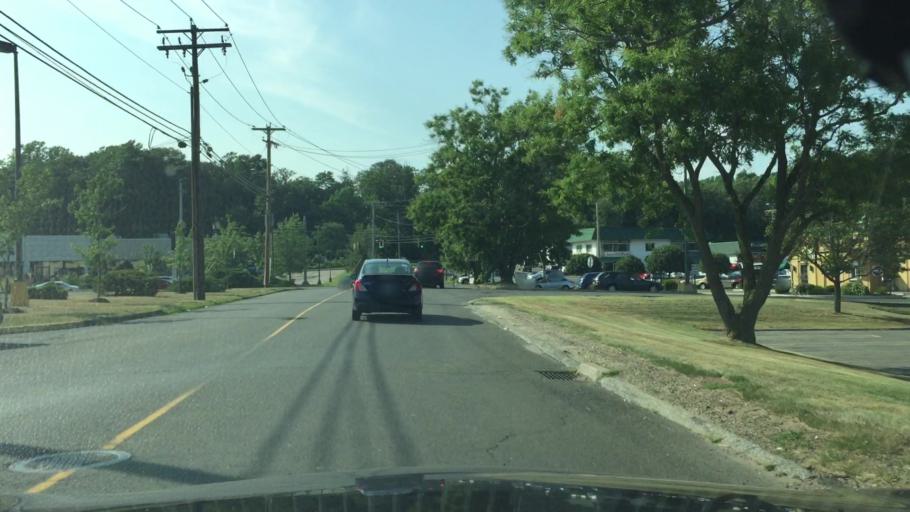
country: US
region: Connecticut
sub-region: New Haven County
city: Orange
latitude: 41.2521
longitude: -73.0178
